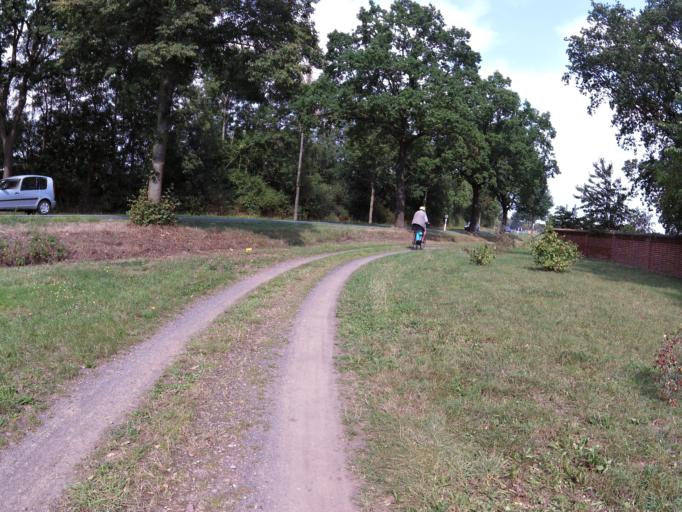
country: DE
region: Lower Saxony
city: Stolzenau
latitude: 52.5288
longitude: 9.0772
